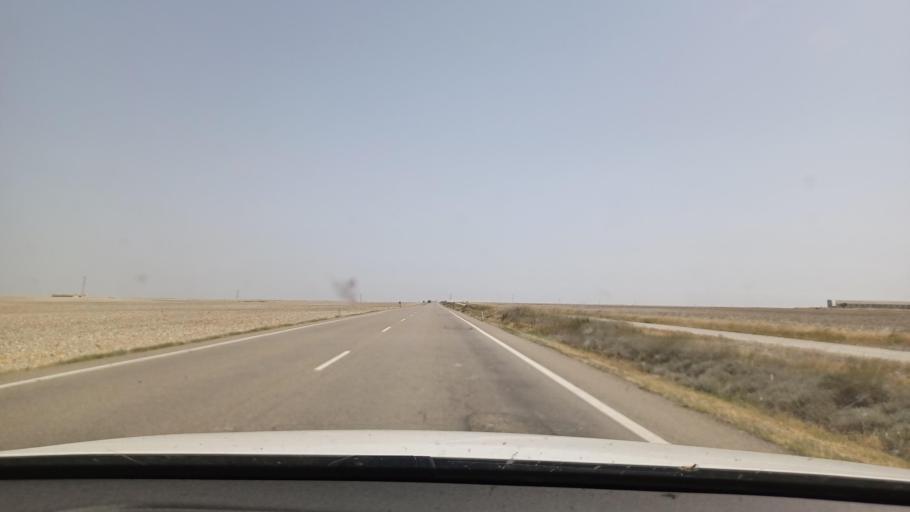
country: ES
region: Aragon
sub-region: Provincia de Zaragoza
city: Bujaraloz
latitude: 41.4540
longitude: -0.1416
